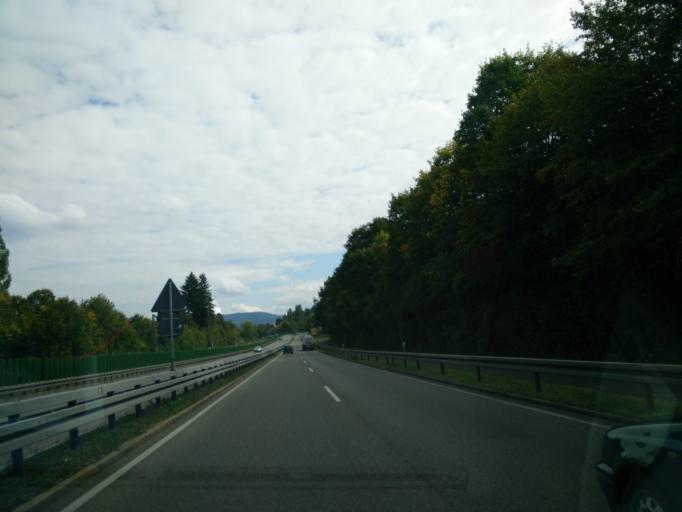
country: DE
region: Baden-Wuerttemberg
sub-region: Tuebingen Region
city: Reutlingen
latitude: 48.4933
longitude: 9.1825
